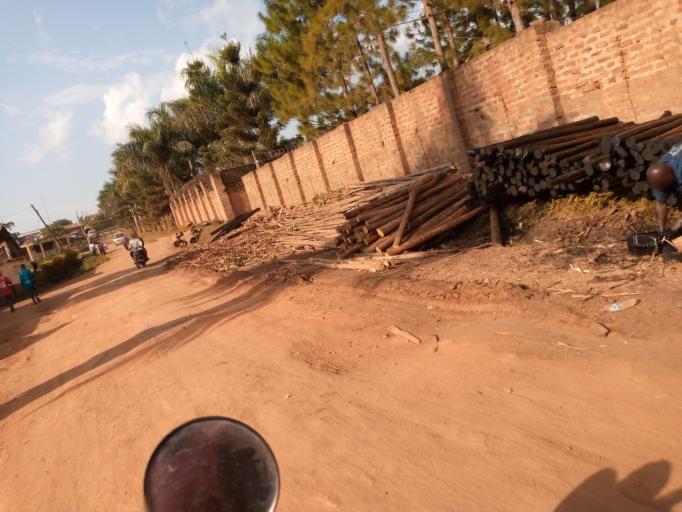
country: UG
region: Eastern Region
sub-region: Mbale District
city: Mbale
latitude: 1.0667
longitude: 34.1761
